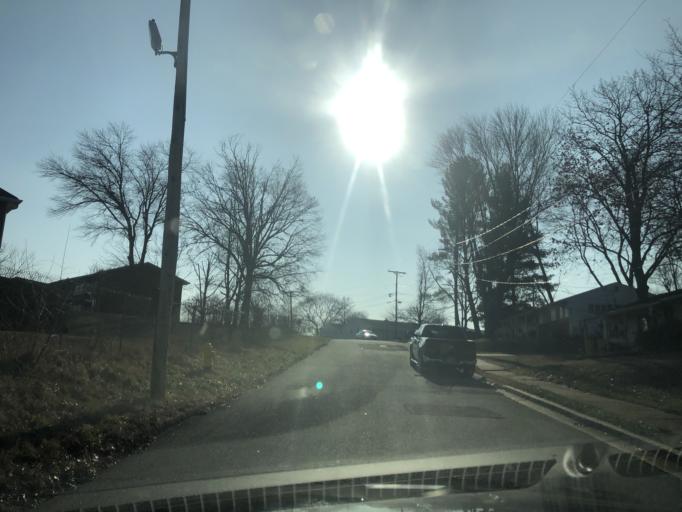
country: US
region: Maryland
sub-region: Anne Arundel County
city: Odenton
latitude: 39.0804
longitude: -76.6957
